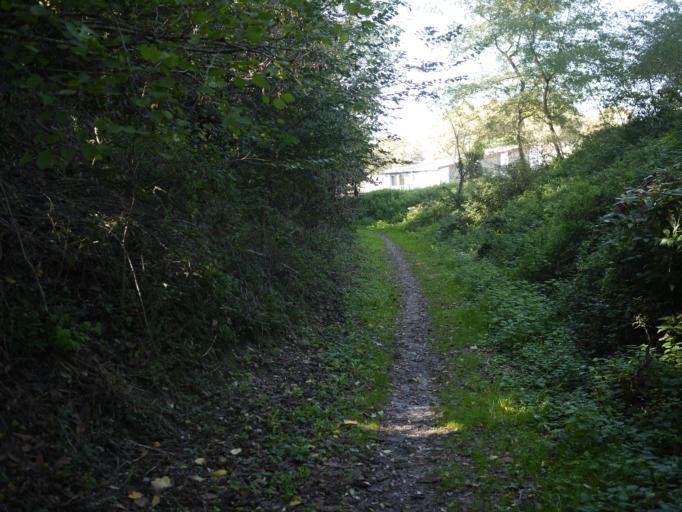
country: FR
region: Aquitaine
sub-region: Departement des Landes
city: Saint-Paul-les-Dax
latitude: 43.7240
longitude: -1.0655
